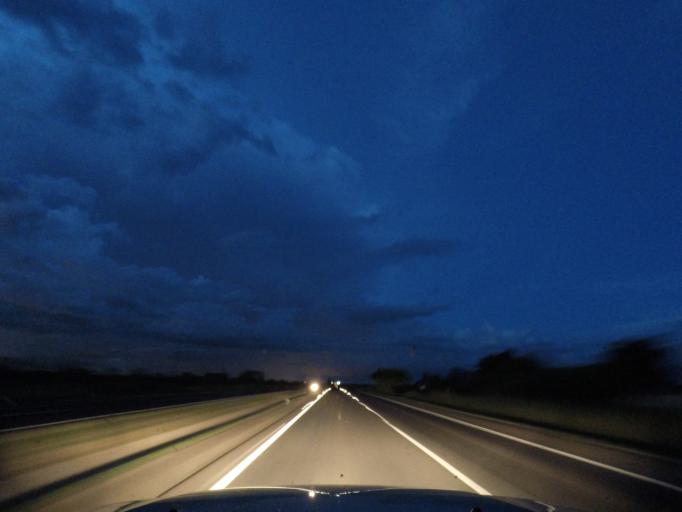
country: BR
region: Minas Gerais
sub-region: Uberlandia
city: Uberlandia
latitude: -19.2131
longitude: -48.1479
